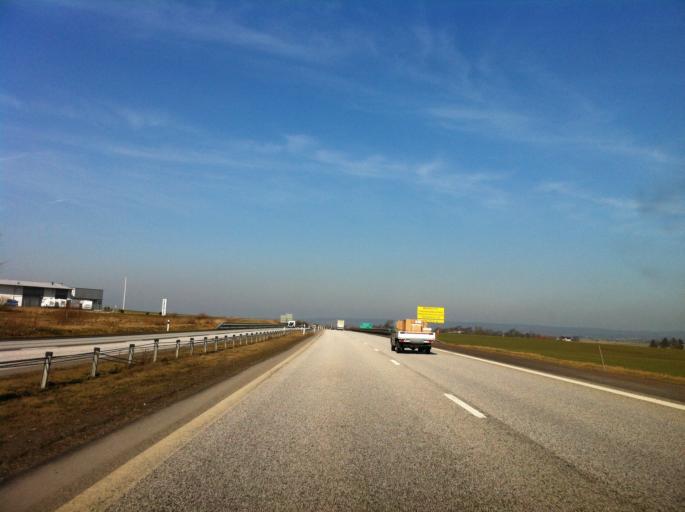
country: SE
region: Skane
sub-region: Angelholms Kommun
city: AEngelholm
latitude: 56.2579
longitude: 12.8973
